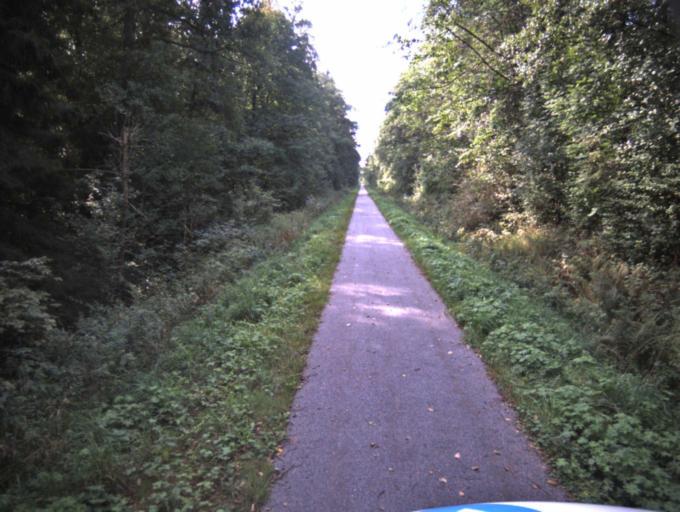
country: SE
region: Vaestra Goetaland
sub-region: Tranemo Kommun
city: Limmared
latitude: 57.6659
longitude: 13.3657
